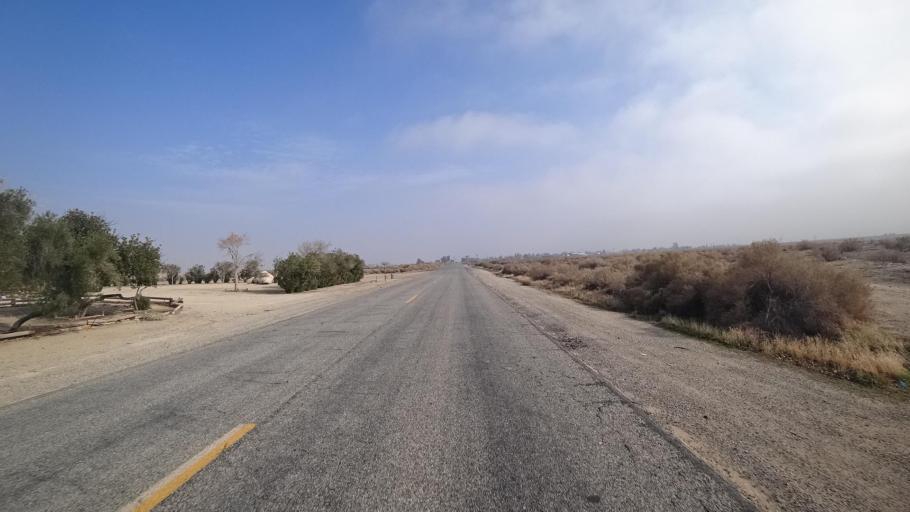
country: US
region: California
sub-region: Kern County
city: Ford City
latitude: 35.2096
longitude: -119.4213
